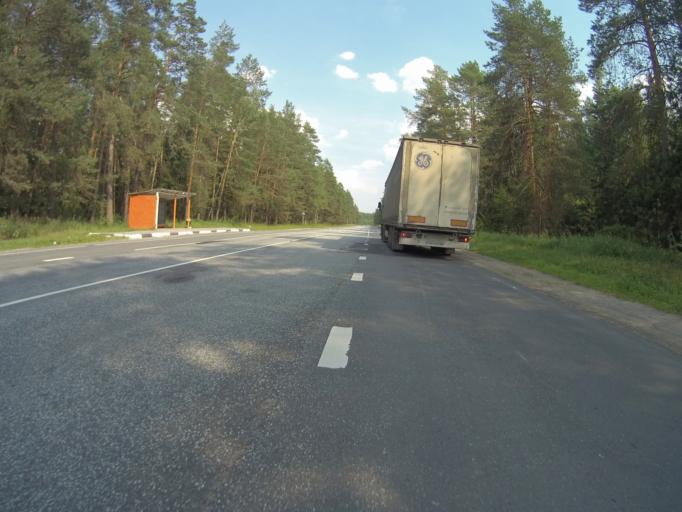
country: RU
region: Vladimir
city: Muromtsevo
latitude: 55.9504
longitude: 41.0224
